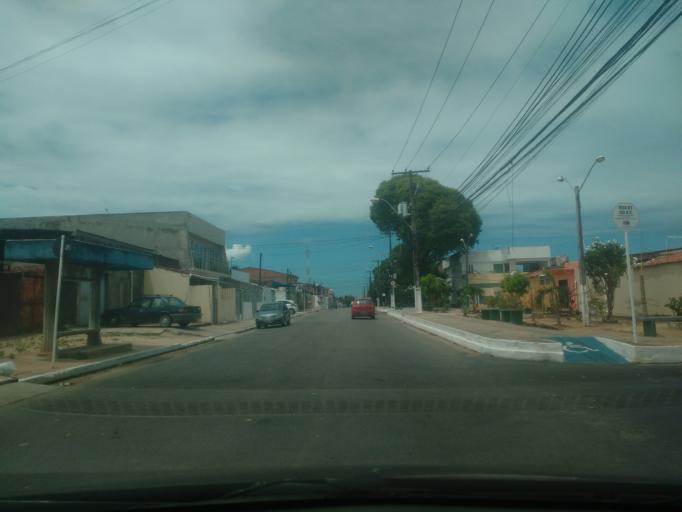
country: BR
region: Alagoas
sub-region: Satuba
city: Satuba
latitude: -9.5545
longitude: -35.7665
